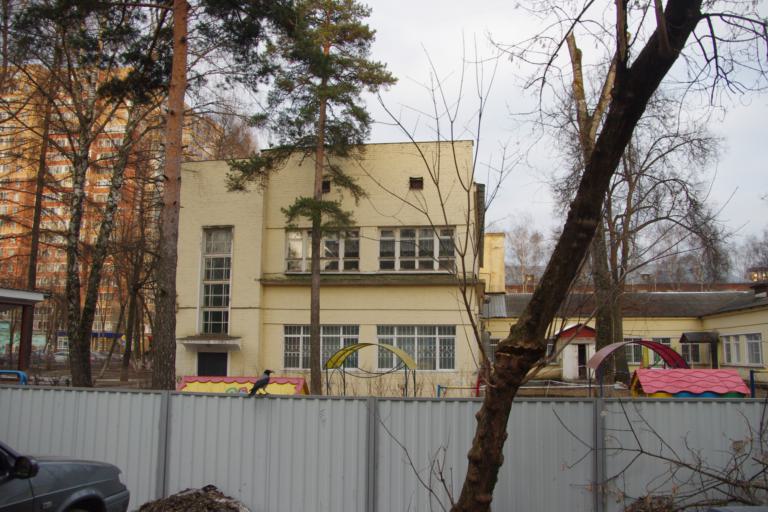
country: RU
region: Moskovskaya
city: Yubileyny
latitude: 55.9153
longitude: 37.8589
